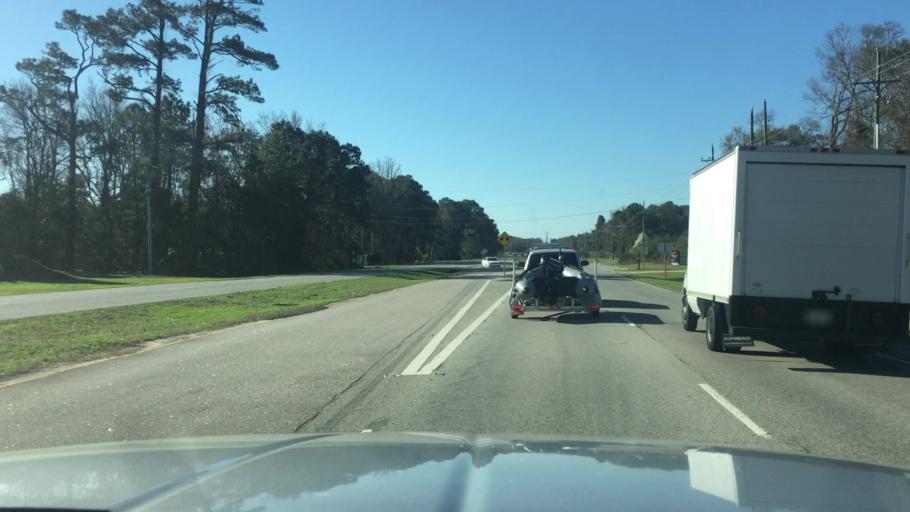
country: US
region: North Carolina
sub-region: New Hanover County
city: Sea Breeze
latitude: 34.0704
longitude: -77.8966
